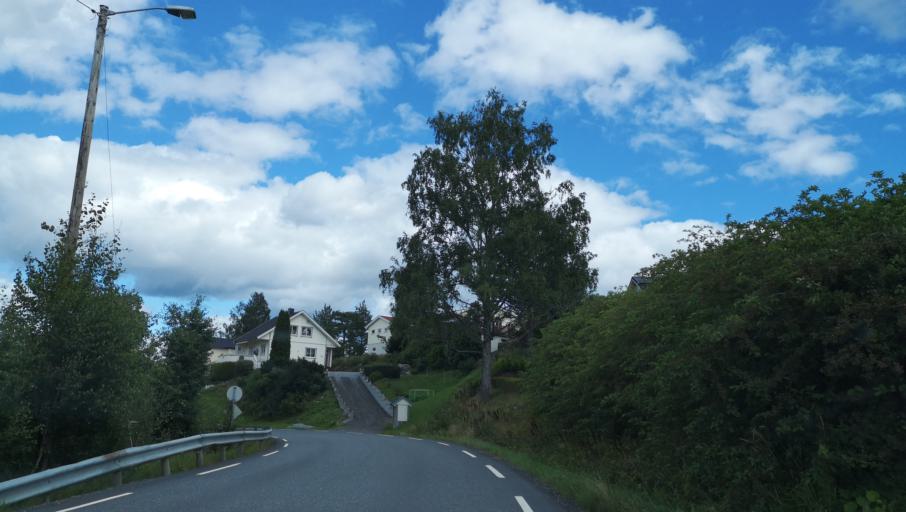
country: NO
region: Ostfold
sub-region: Hobol
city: Tomter
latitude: 59.6681
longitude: 11.0041
